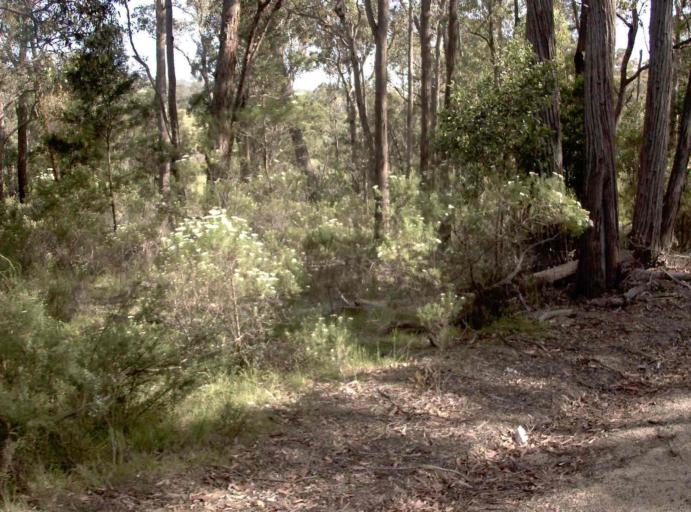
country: AU
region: Victoria
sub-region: East Gippsland
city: Lakes Entrance
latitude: -37.5512
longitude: 148.1469
